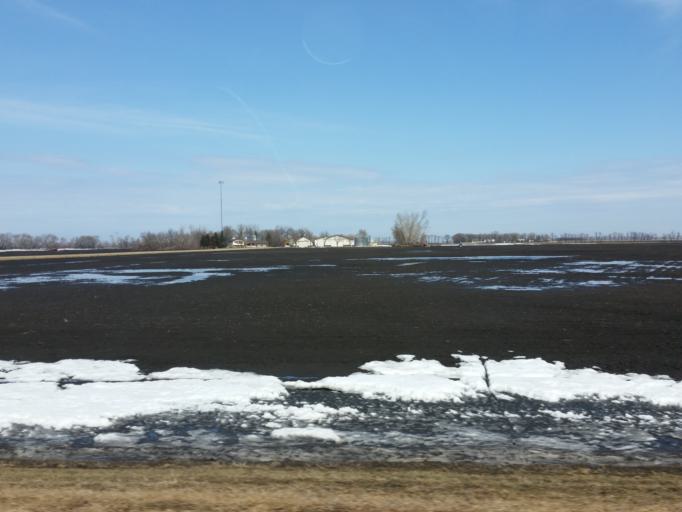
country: US
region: North Dakota
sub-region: Walsh County
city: Grafton
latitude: 48.2954
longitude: -97.2174
